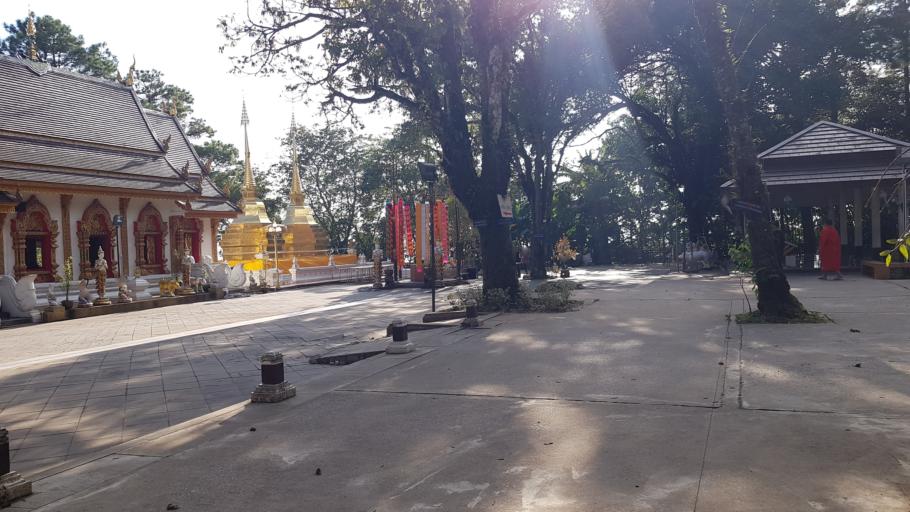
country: TH
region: Chiang Rai
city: Mae Fa Luang
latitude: 20.3246
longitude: 99.8331
